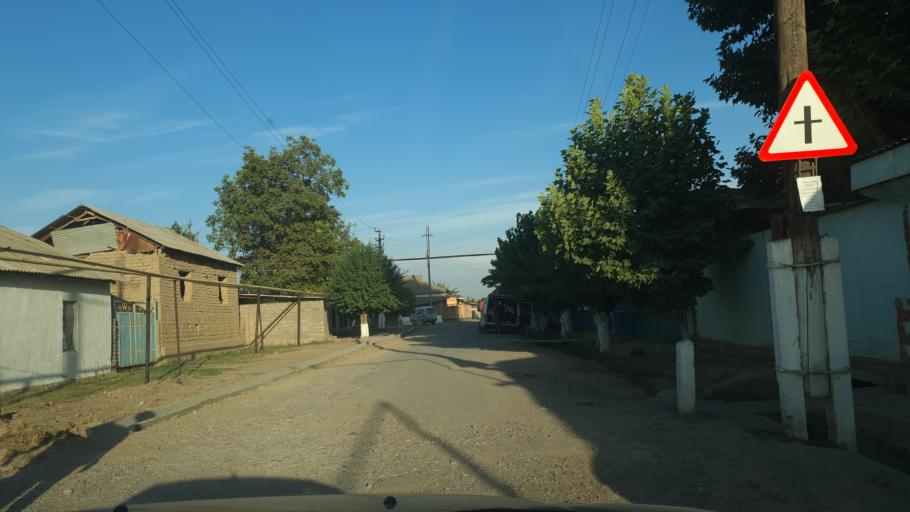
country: UZ
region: Toshkent
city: Tuytepa
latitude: 41.1033
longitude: 69.4007
